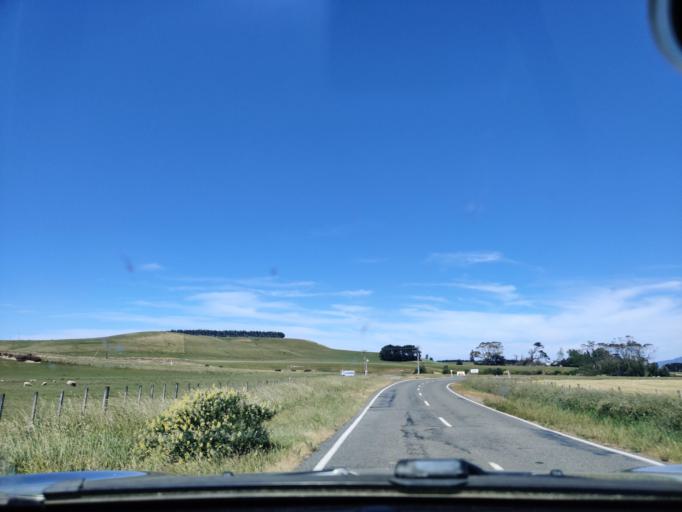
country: NZ
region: Wellington
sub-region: Upper Hutt City
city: Upper Hutt
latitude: -41.3709
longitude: 175.1761
